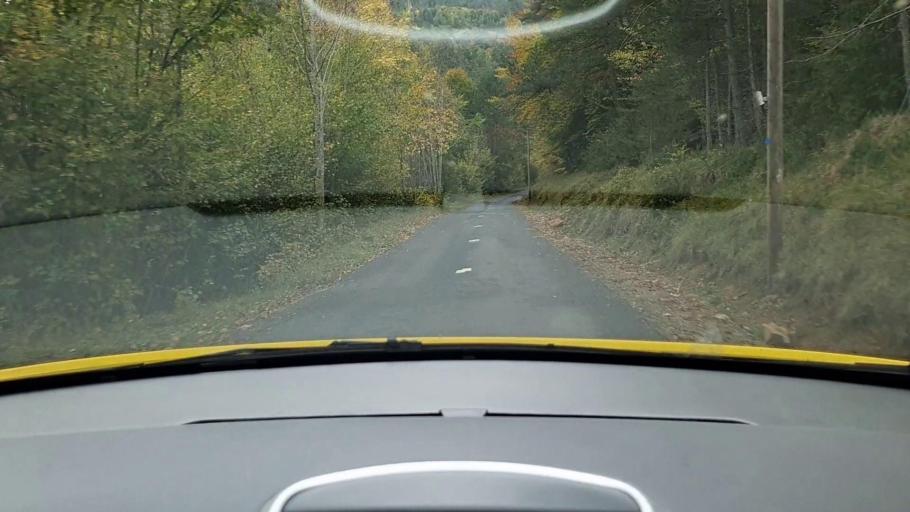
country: FR
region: Languedoc-Roussillon
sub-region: Departement de la Lozere
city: Meyrueis
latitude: 44.1204
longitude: 3.4339
